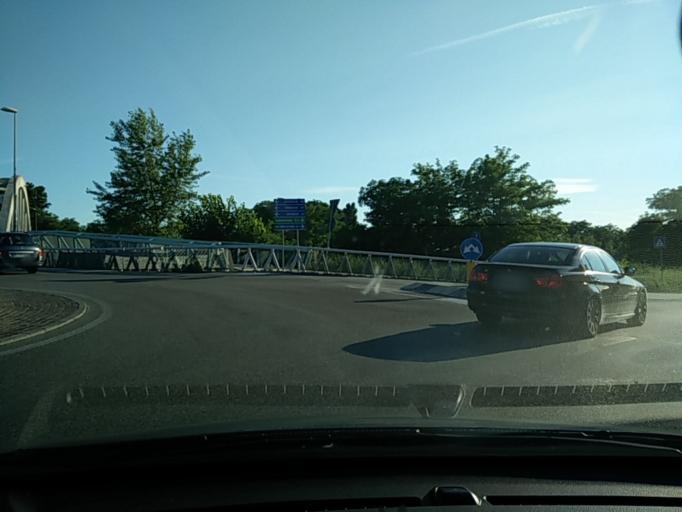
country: IT
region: Veneto
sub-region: Provincia di Venezia
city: Eraclea
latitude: 45.5743
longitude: 12.6743
